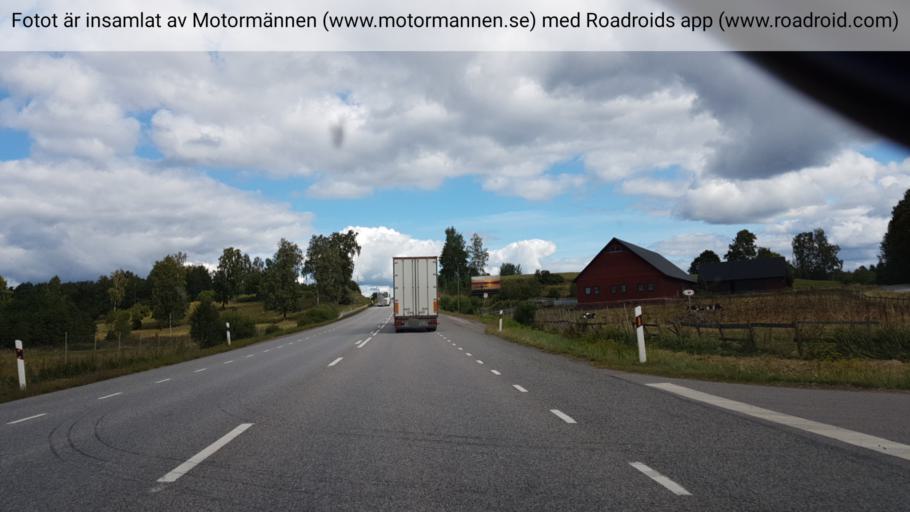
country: SE
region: Joenkoeping
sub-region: Tranas Kommun
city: Tranas
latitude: 58.0072
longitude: 14.9274
